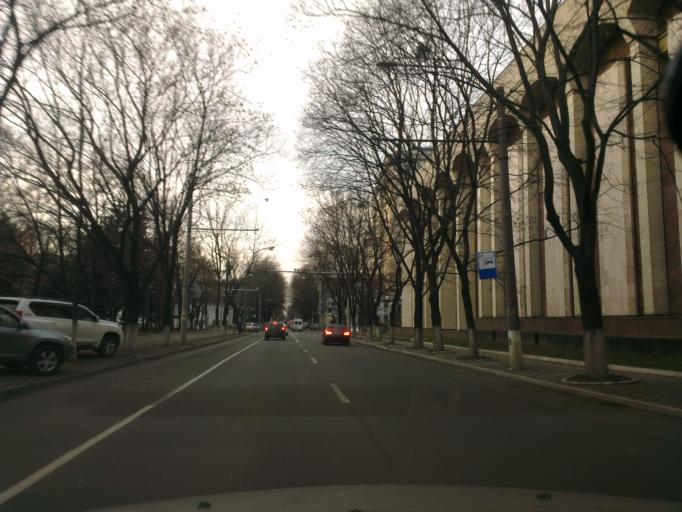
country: MD
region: Chisinau
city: Chisinau
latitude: 47.0238
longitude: 28.8248
